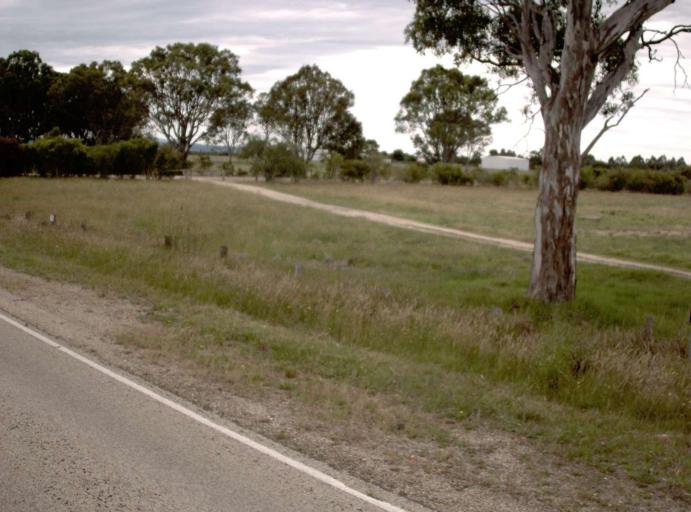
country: AU
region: Victoria
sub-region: East Gippsland
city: Bairnsdale
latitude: -37.8792
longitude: 147.5592
